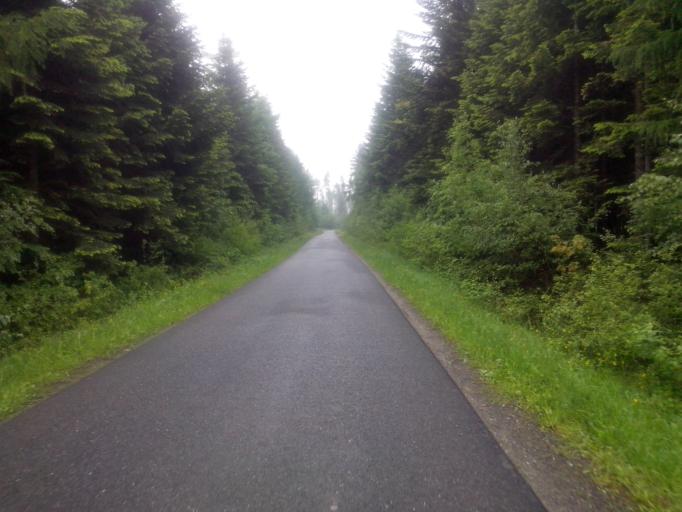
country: PL
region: Subcarpathian Voivodeship
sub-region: Powiat strzyzowski
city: Wysoka Strzyzowska
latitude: 49.8169
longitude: 21.7880
